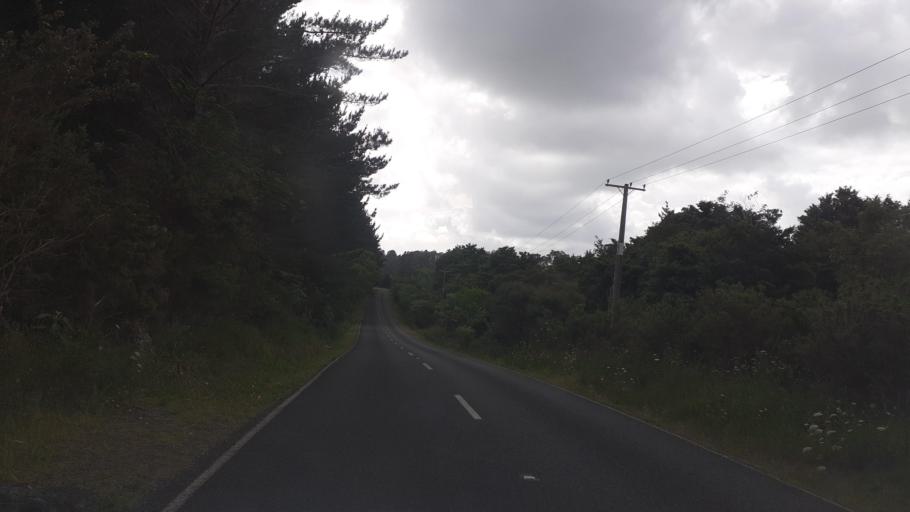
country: NZ
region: Northland
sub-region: Far North District
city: Kerikeri
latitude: -35.2254
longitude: 174.0176
